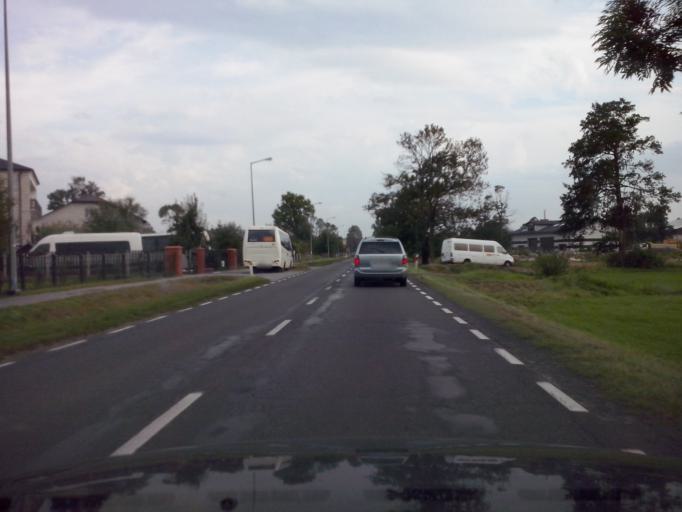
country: PL
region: Lublin Voivodeship
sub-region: Powiat bilgorajski
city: Bilgoraj
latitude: 50.5044
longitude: 22.7217
